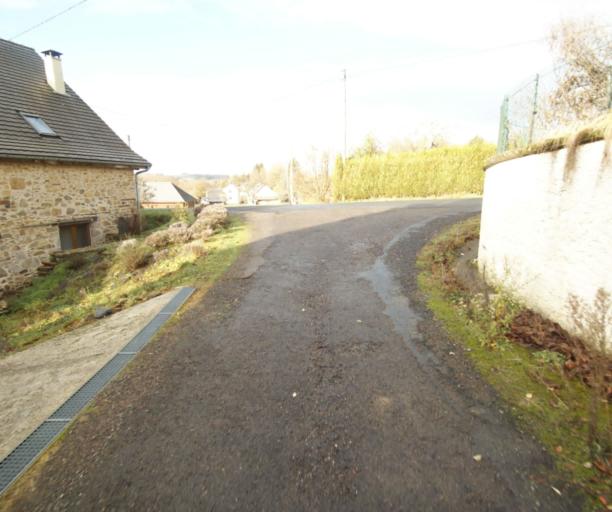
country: FR
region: Limousin
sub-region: Departement de la Correze
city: Saint-Mexant
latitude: 45.2763
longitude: 1.6060
